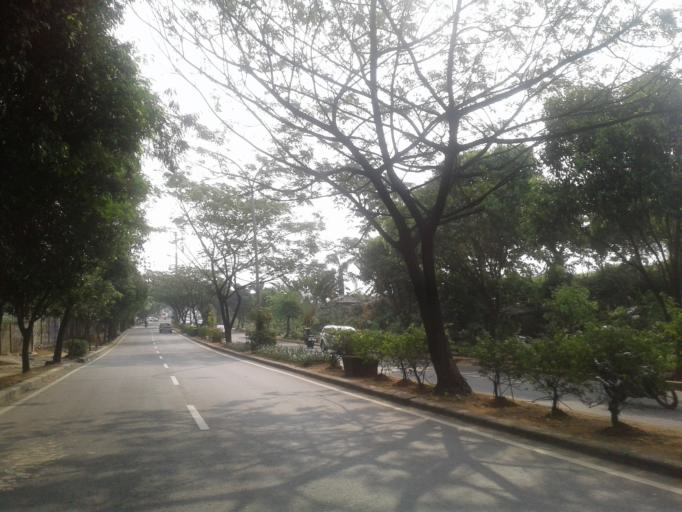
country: ID
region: West Java
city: Depok
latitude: -6.3817
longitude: 106.8629
